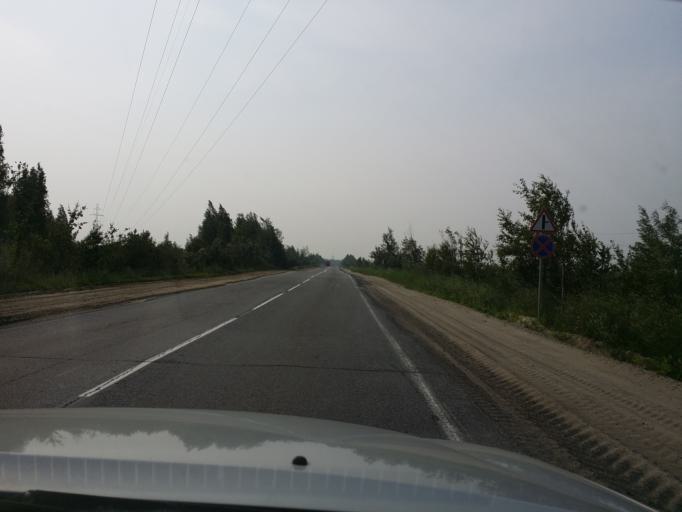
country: RU
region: Khanty-Mansiyskiy Avtonomnyy Okrug
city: Nizhnevartovsk
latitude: 61.0991
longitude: 76.6384
